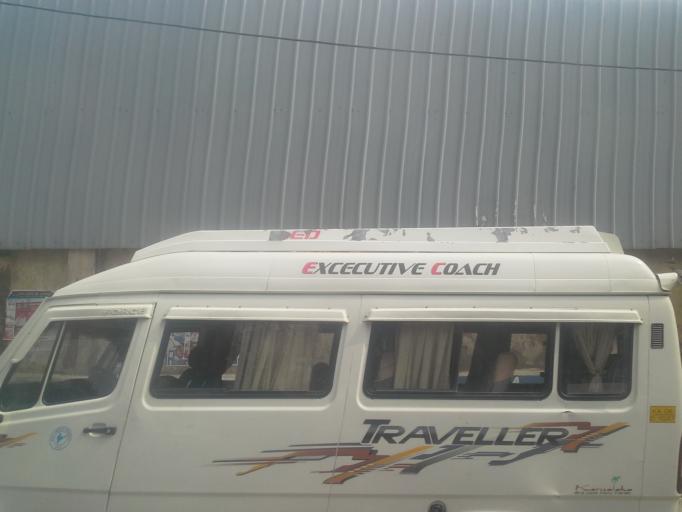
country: IN
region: Karnataka
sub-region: Bangalore Urban
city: Bangalore
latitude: 12.9828
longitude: 77.5767
